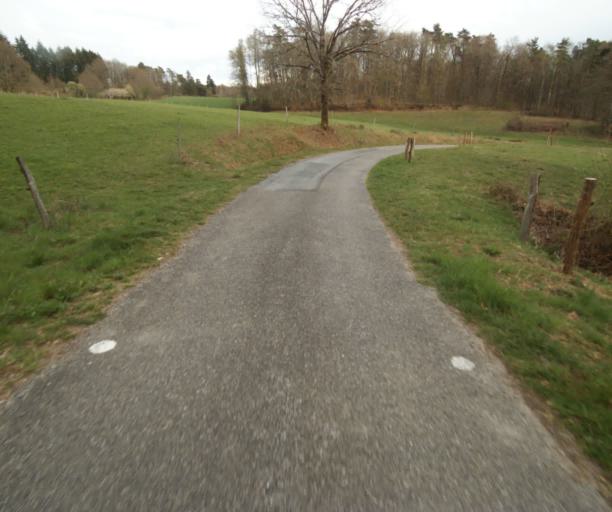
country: FR
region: Limousin
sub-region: Departement de la Correze
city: Argentat
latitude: 45.2013
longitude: 1.9876
